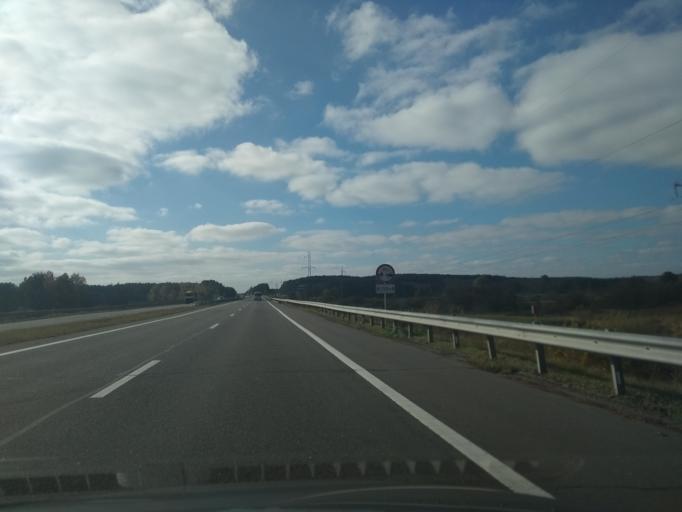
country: BY
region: Minsk
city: Novy Svyerzhan'
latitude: 53.4995
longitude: 26.6536
